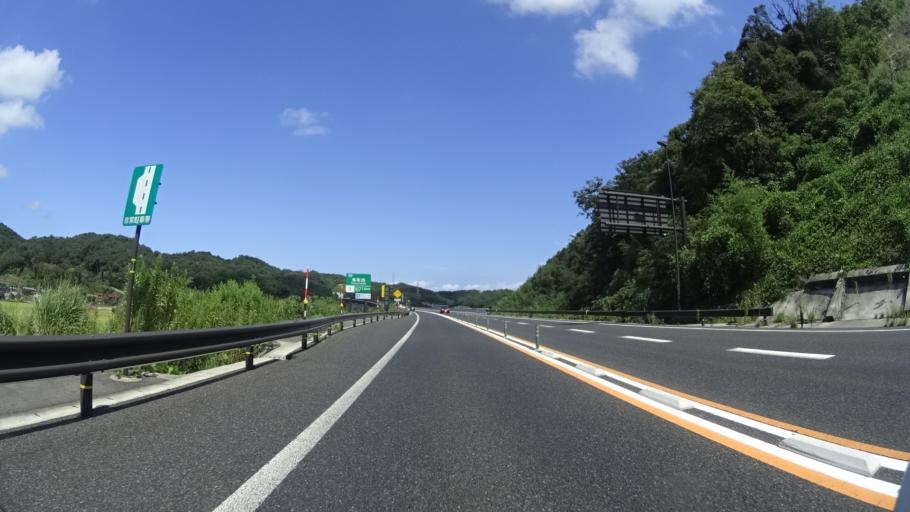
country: JP
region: Tottori
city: Tottori
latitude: 35.4821
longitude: 134.1979
